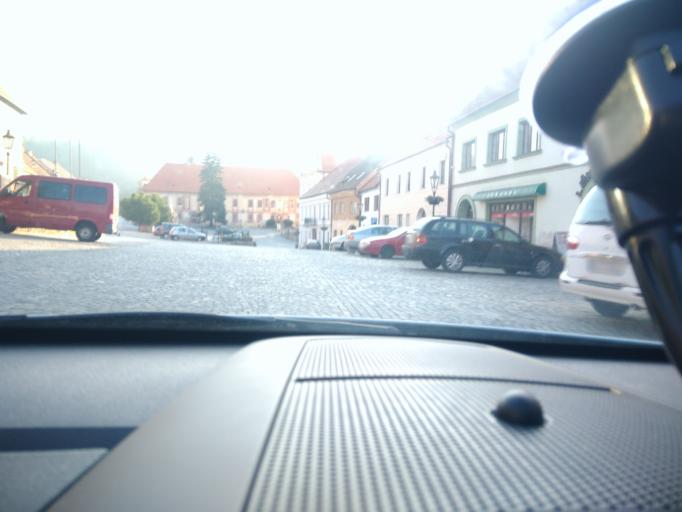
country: CZ
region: Vysocina
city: Namest' nad Oslavou
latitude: 49.2059
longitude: 16.1564
